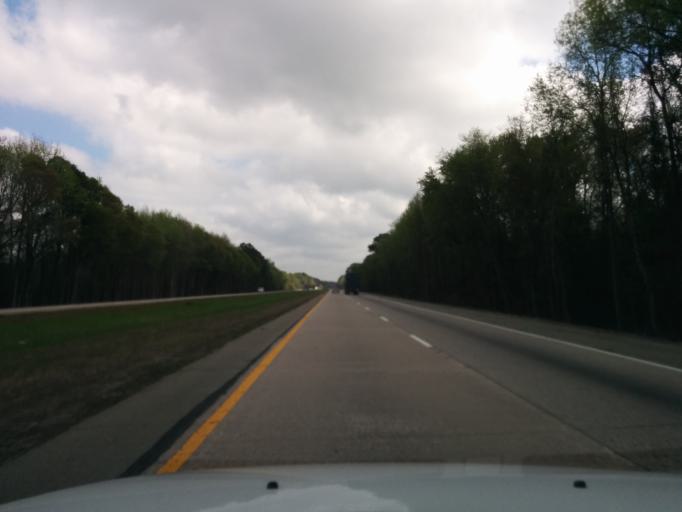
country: US
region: Georgia
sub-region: Bryan County
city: Pembroke
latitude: 32.2158
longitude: -81.5236
